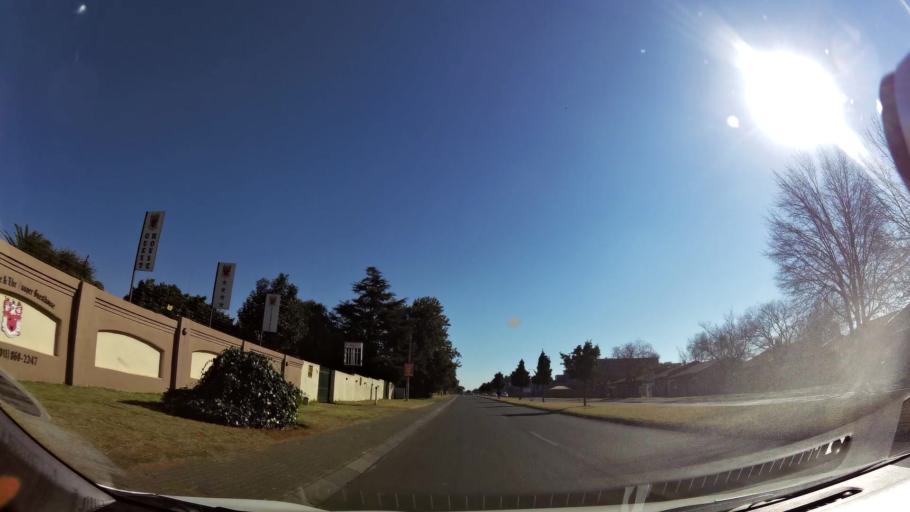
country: ZA
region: Gauteng
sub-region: Ekurhuleni Metropolitan Municipality
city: Germiston
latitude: -26.3295
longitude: 28.0989
